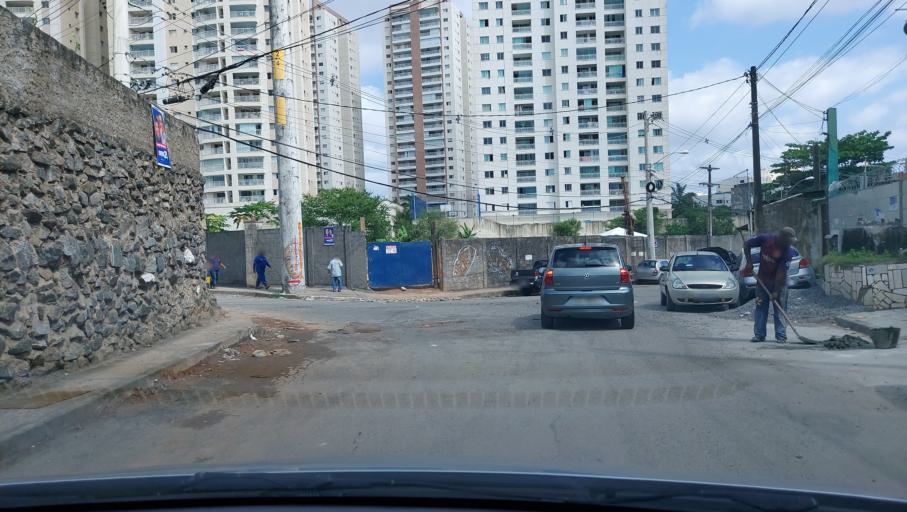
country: BR
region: Bahia
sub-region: Salvador
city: Salvador
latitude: -12.9654
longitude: -38.4301
